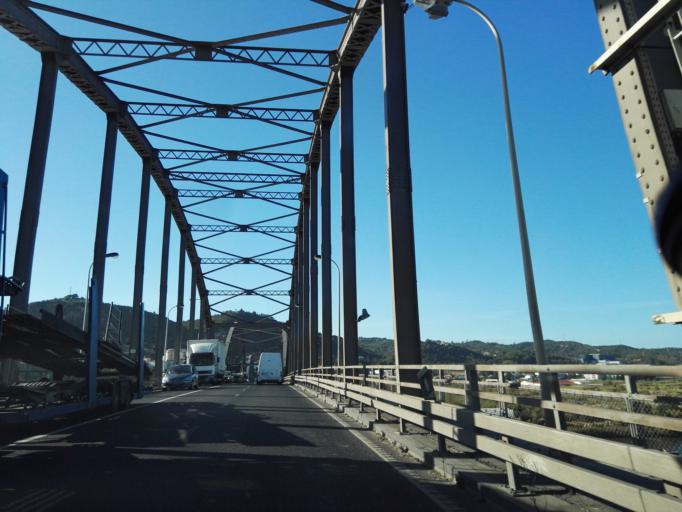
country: PT
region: Lisbon
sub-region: Vila Franca de Xira
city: Vila Franca de Xira
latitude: 38.9560
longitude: -8.9783
